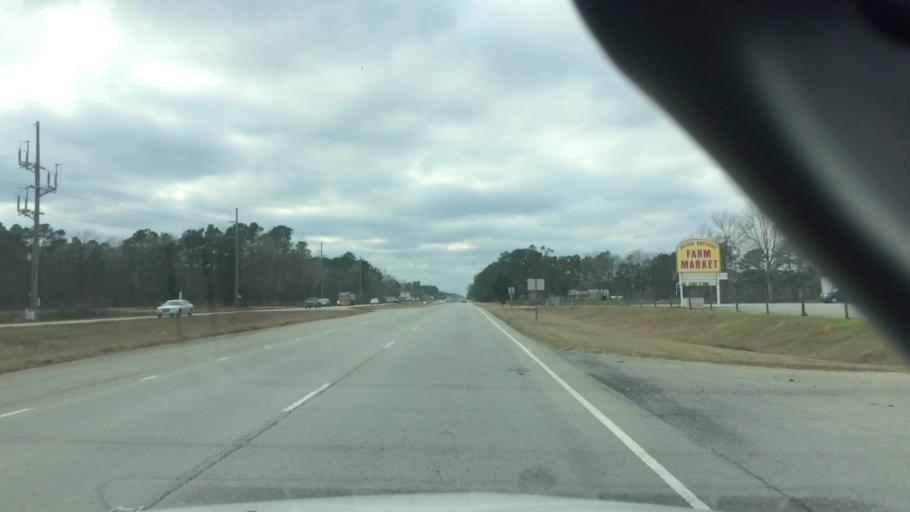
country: US
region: North Carolina
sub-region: Brunswick County
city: Shallotte
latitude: 33.9544
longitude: -78.4507
